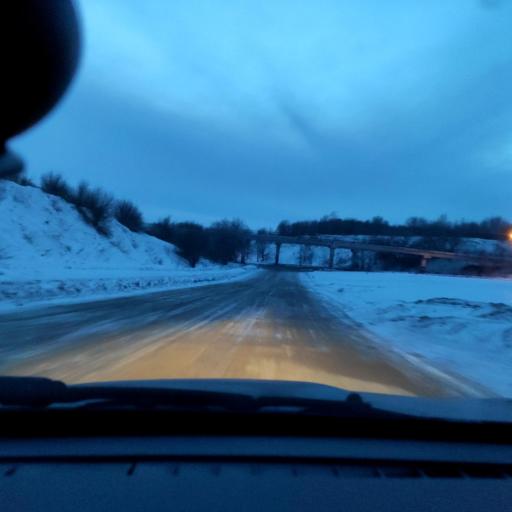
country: RU
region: Samara
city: Tol'yatti
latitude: 53.4970
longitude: 49.2718
